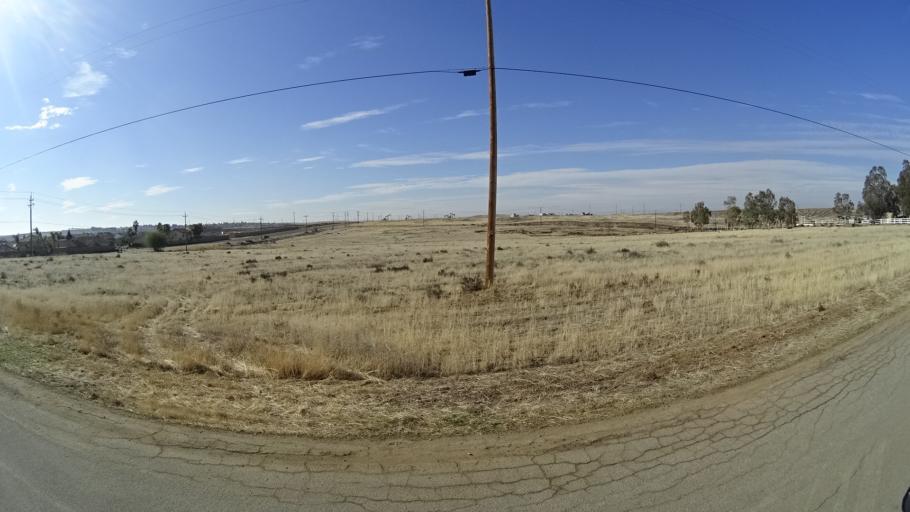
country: US
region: California
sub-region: Kern County
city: Oildale
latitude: 35.4136
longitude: -118.8983
